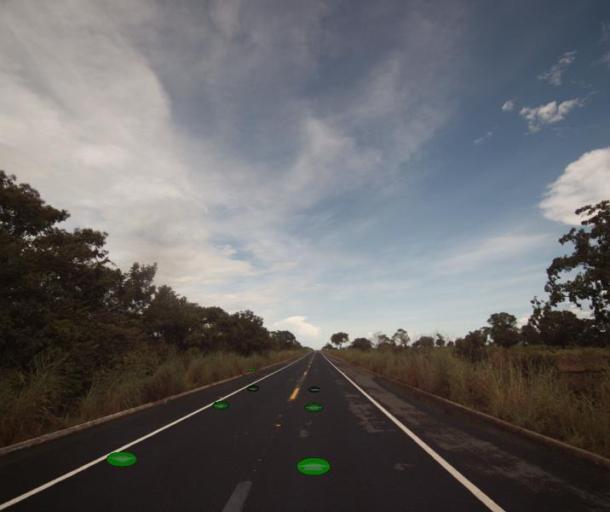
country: BR
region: Goias
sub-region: Sao Miguel Do Araguaia
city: Sao Miguel do Araguaia
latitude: -13.2742
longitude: -50.5026
